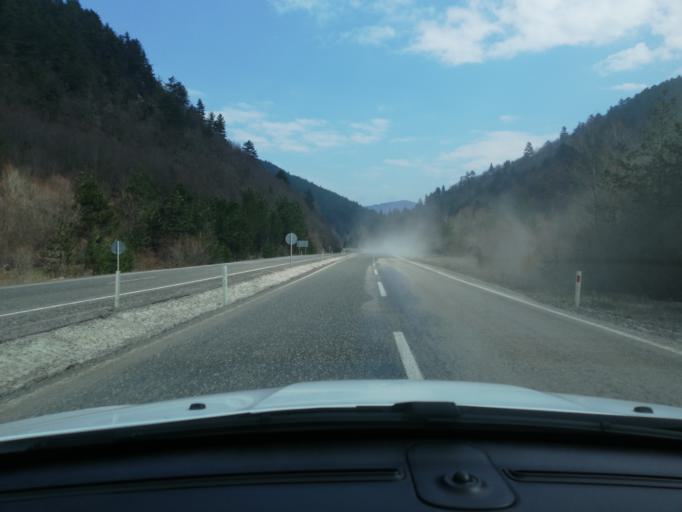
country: TR
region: Kastamonu
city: Kuzyaka
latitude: 41.1455
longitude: 33.7812
